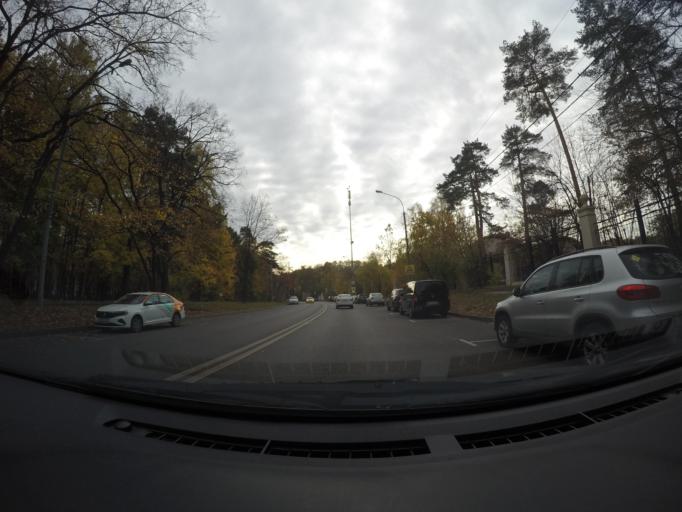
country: RU
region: Moscow
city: Sokol'niki
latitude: 55.8045
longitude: 37.6841
